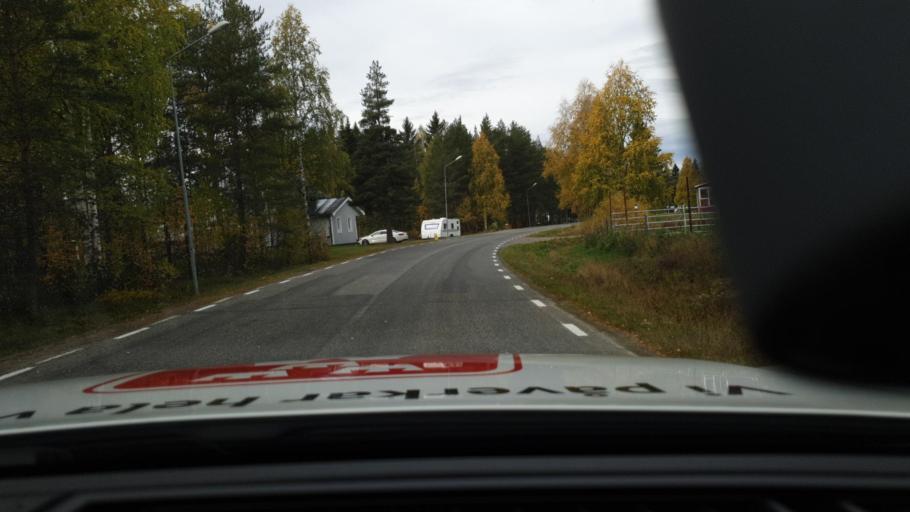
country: SE
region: Vaesterbotten
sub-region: Skelleftea Kommun
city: Langsele
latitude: 64.9468
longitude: 19.9375
